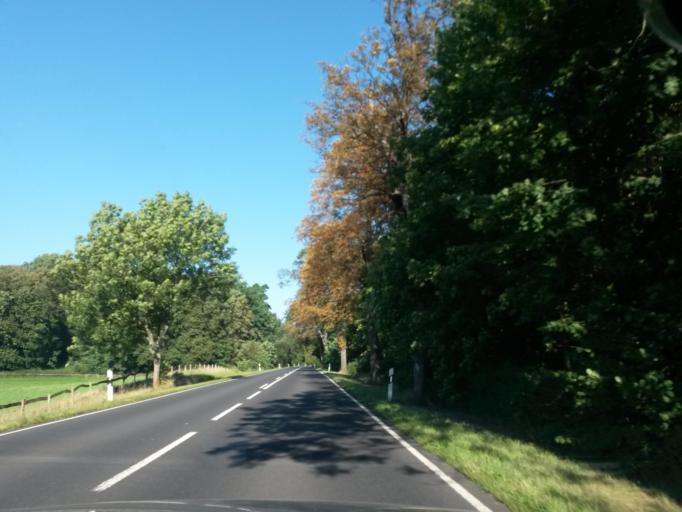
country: DE
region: Brandenburg
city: Angermunde
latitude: 53.0590
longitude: 13.9697
